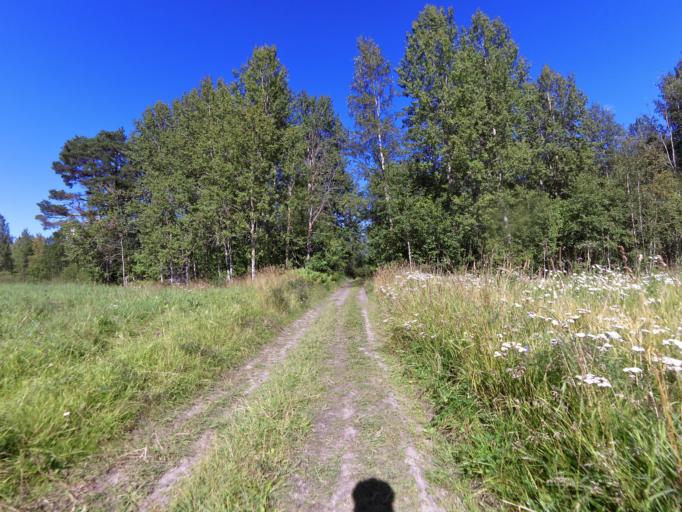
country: SE
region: Gaevleborg
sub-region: Hofors Kommun
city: Hofors
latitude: 60.5269
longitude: 16.4098
